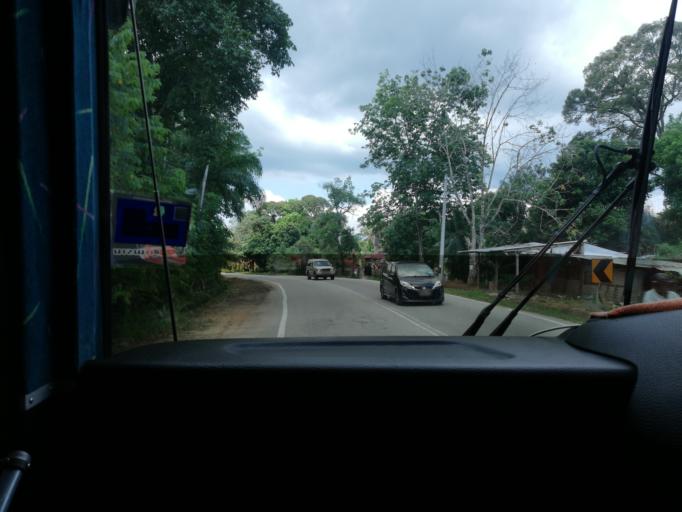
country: MY
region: Perak
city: Parit Buntar
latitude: 5.1357
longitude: 100.5841
